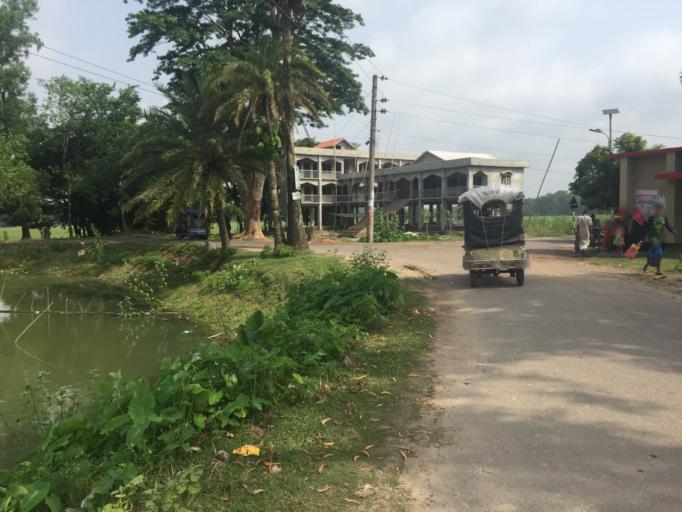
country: BD
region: Barisal
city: Mathba
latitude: 22.2454
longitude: 89.9131
